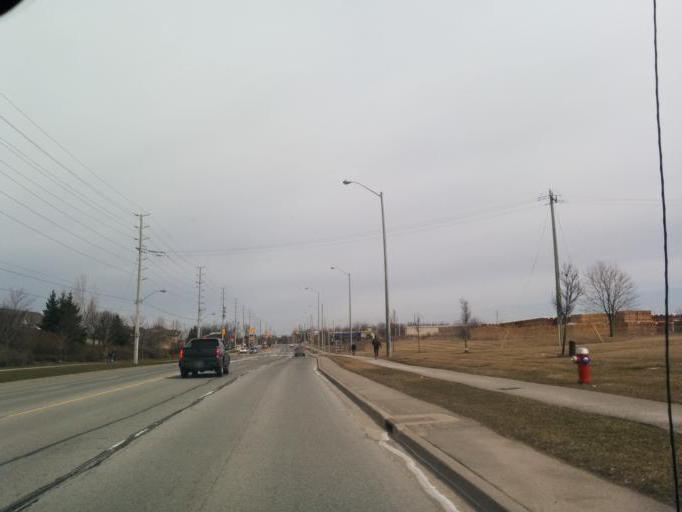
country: CA
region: Ontario
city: Brampton
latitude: 43.7228
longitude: -79.8172
